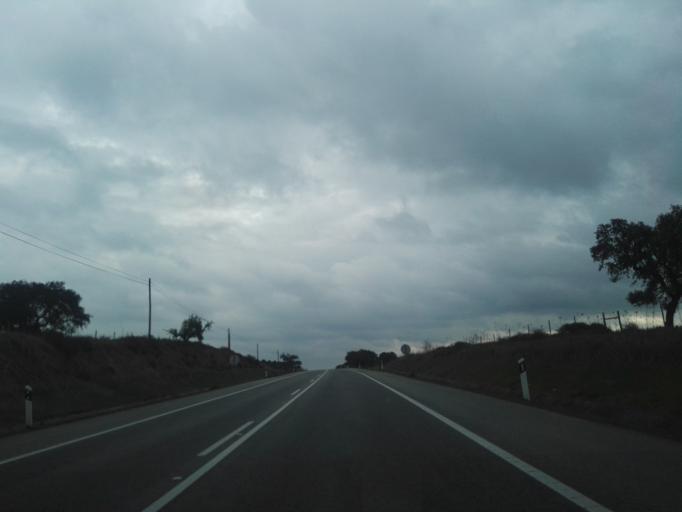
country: PT
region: Portalegre
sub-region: Arronches
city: Arronches
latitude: 39.1518
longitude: -7.3118
